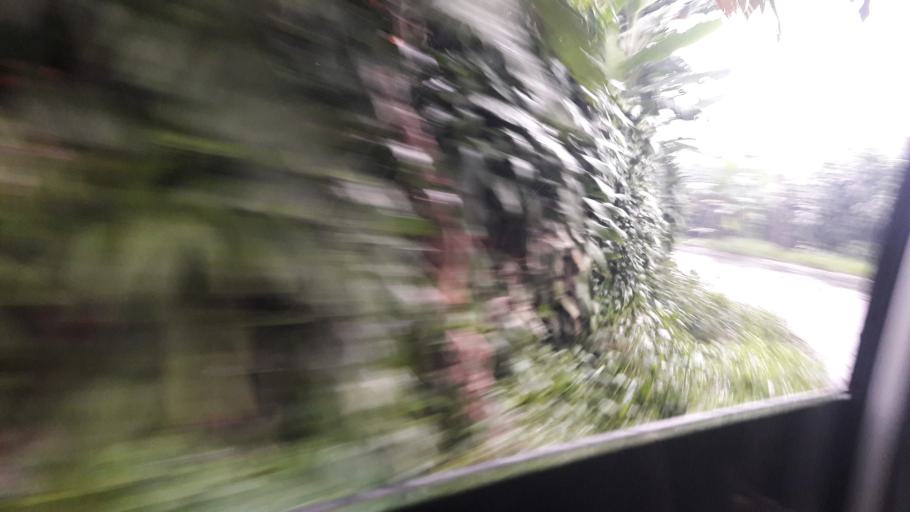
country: ID
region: West Java
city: Cipeundeuy
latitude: -6.6510
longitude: 106.5205
